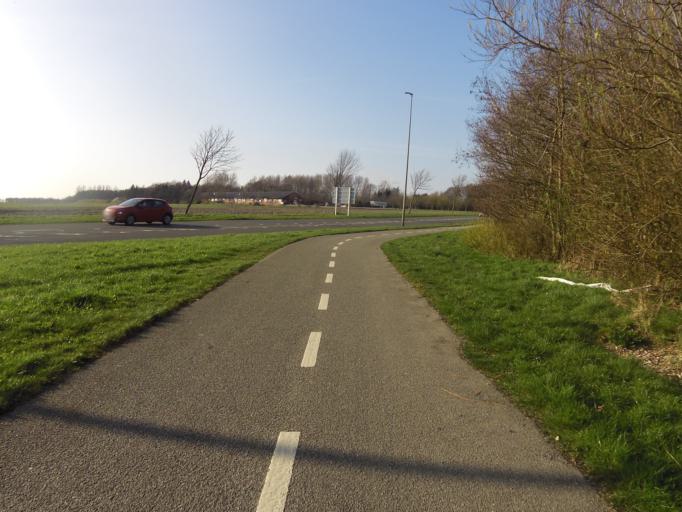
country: DK
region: South Denmark
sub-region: Vejen Kommune
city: Vejen
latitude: 55.4819
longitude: 9.1247
